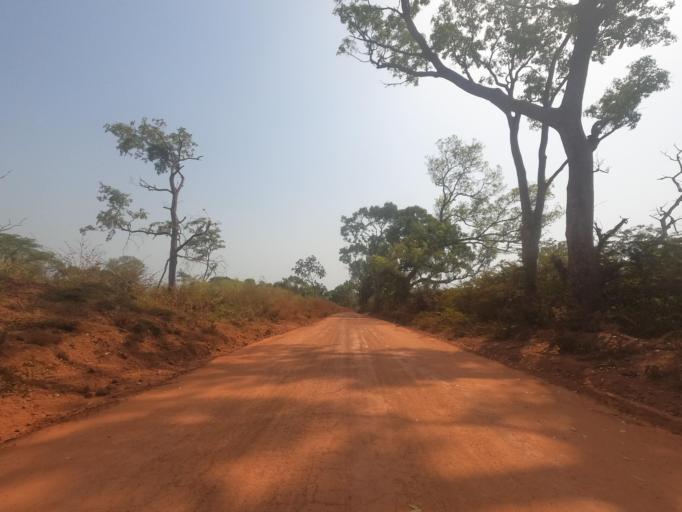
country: GW
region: Oio
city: Bissora
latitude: 12.4560
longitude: -15.4590
